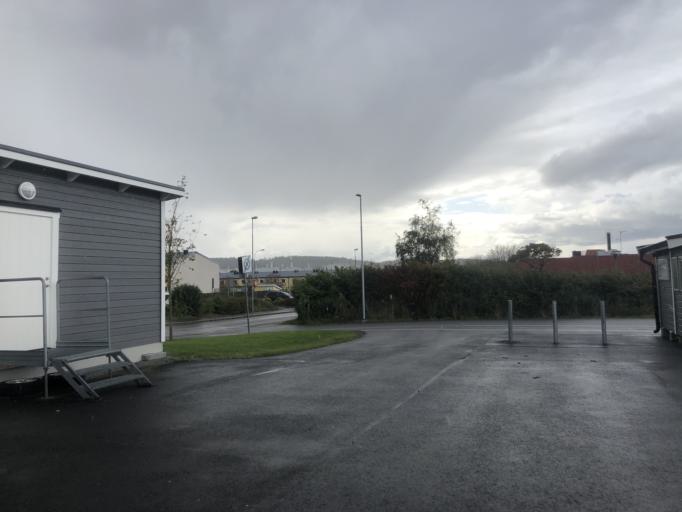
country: SE
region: Vaestra Goetaland
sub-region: Molndal
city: Moelndal
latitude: 57.6506
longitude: 12.0272
